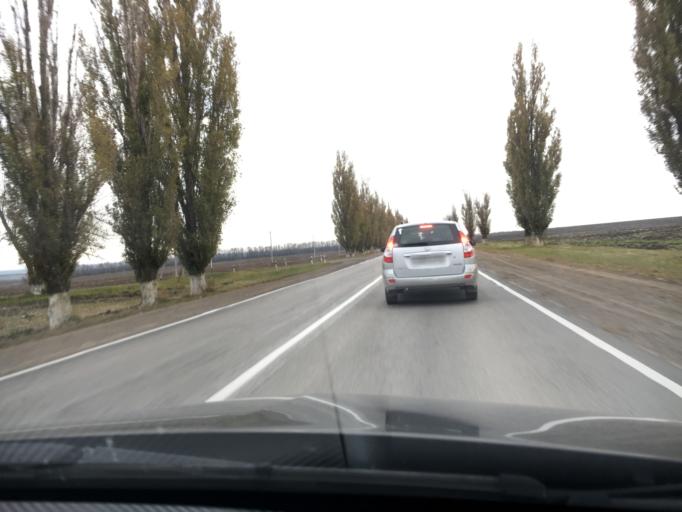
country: RU
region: Rostov
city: Pokrovskoye
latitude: 47.3654
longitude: 38.9914
